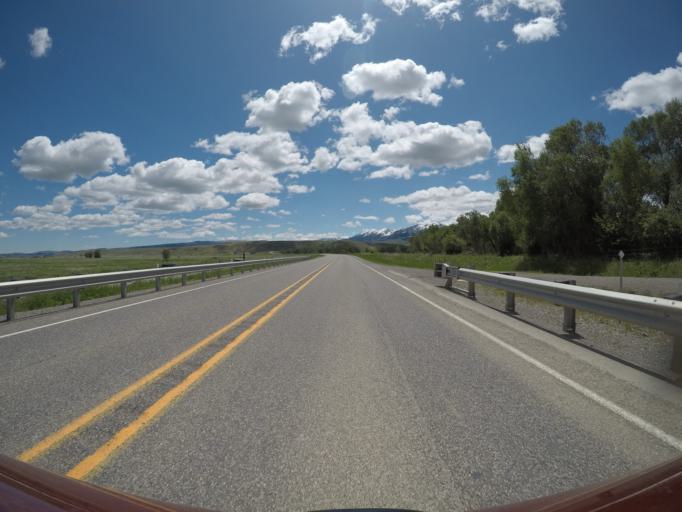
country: US
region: Montana
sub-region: Park County
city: Livingston
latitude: 45.7173
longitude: -110.4671
